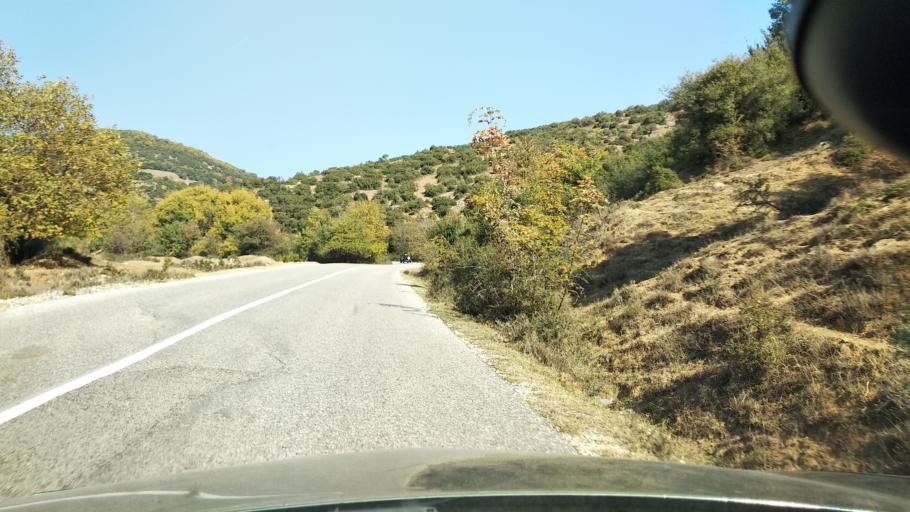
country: GR
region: Thessaly
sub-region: Trikala
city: Kalampaka
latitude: 39.7144
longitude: 21.6493
